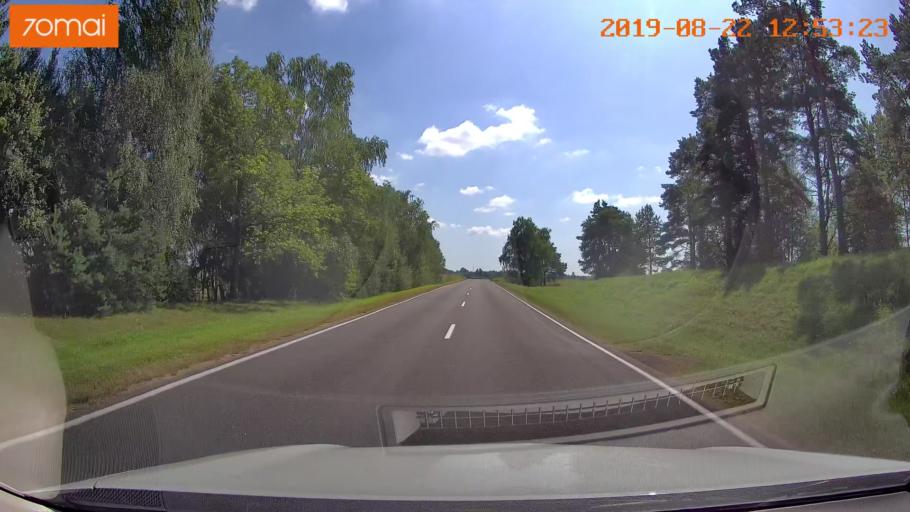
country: BY
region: Minsk
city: Prawdzinski
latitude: 53.4471
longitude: 27.6857
